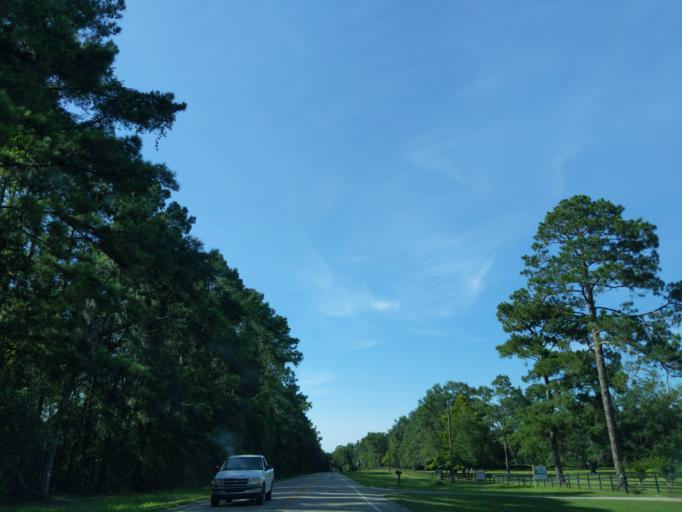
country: US
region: Florida
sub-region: Leon County
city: Woodville
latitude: 30.2789
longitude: -84.3124
